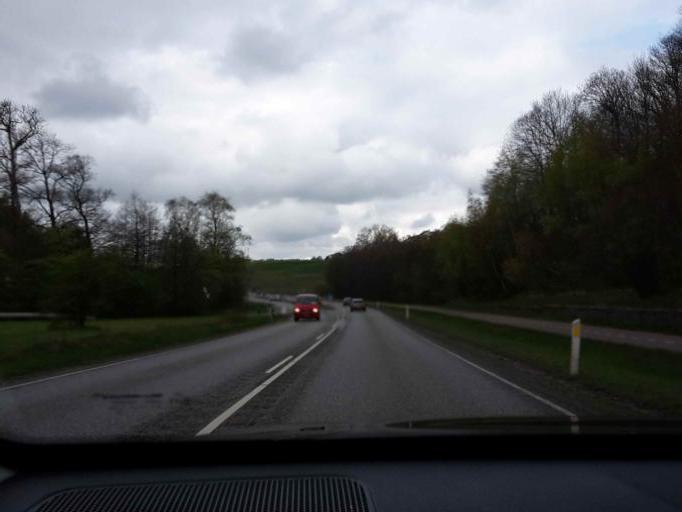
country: DK
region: South Denmark
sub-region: Vejle Kommune
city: Jelling
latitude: 55.7027
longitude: 9.4291
